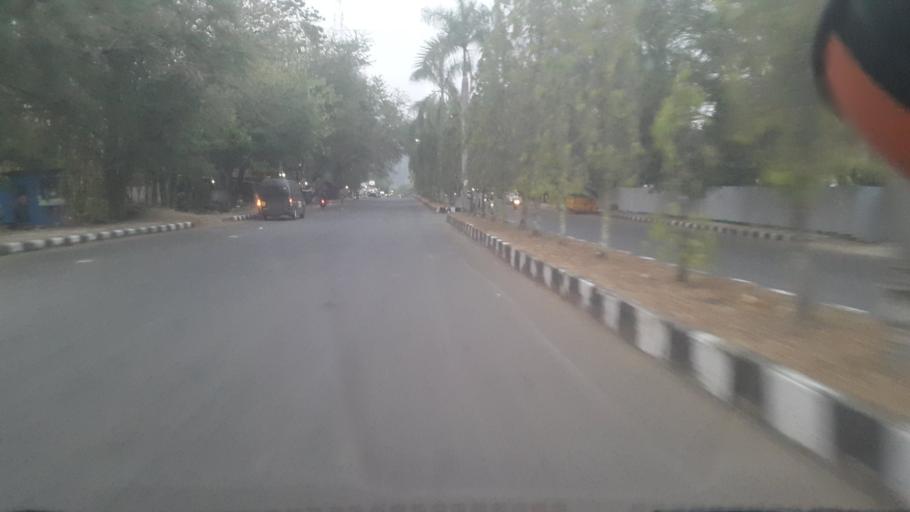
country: ID
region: West Java
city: Pelabuhanratu
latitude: -6.9909
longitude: 106.5568
